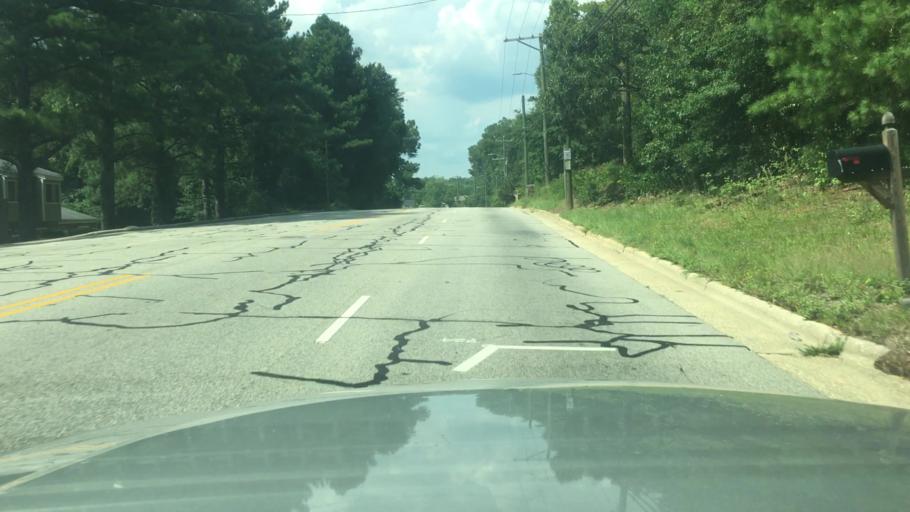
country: US
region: North Carolina
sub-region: Cumberland County
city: Fayetteville
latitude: 35.0847
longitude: -78.8830
